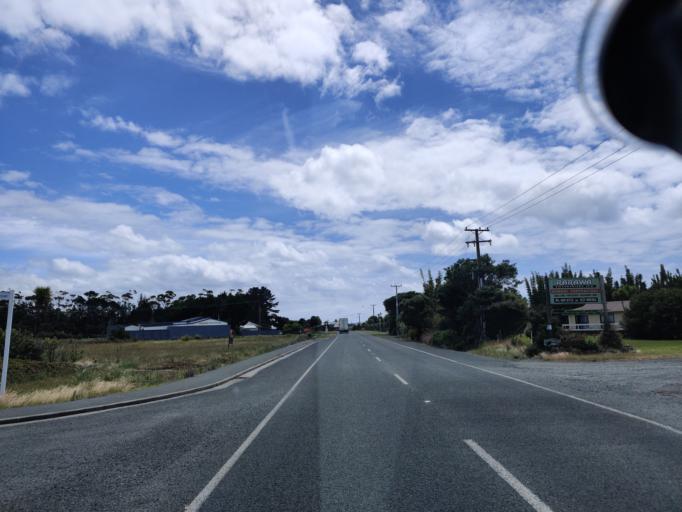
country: NZ
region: Northland
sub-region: Far North District
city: Kaitaia
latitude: -34.8260
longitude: 173.1281
